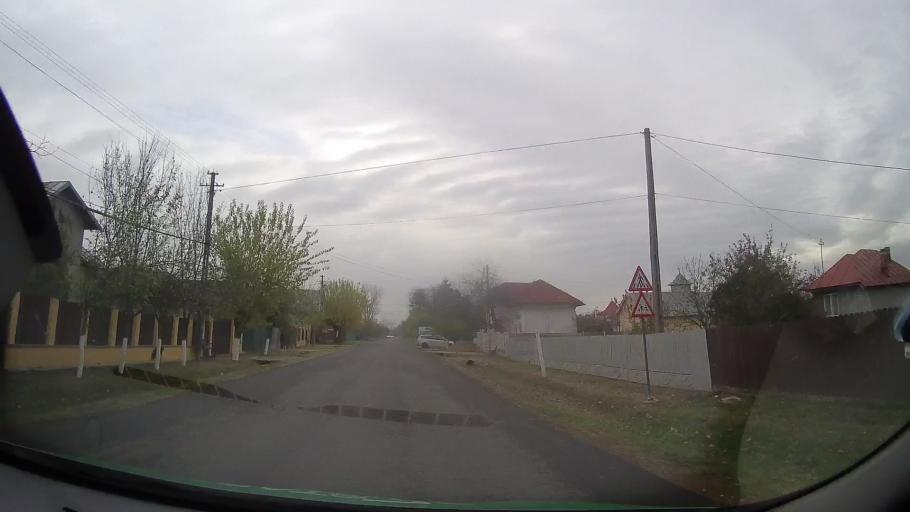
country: RO
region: Prahova
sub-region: Comuna Valea Calugareasca
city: Pantazi
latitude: 44.9209
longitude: 26.1555
